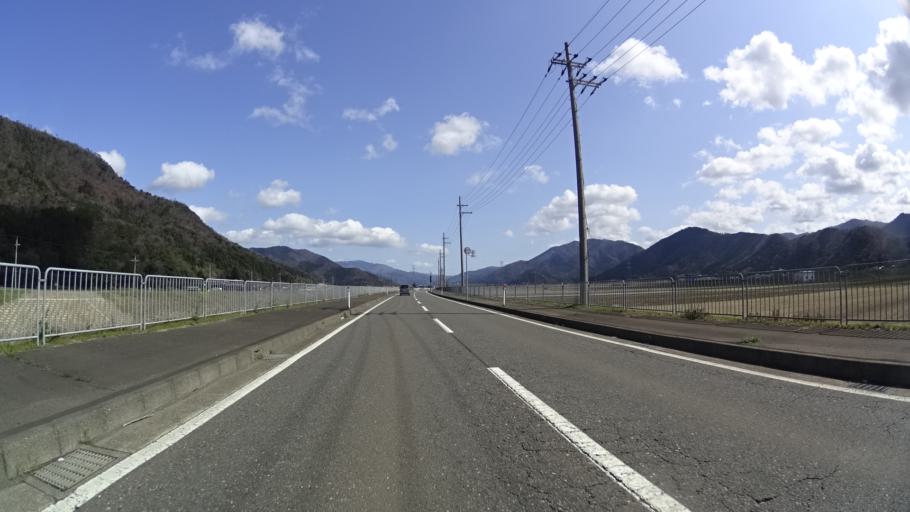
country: JP
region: Fukui
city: Obama
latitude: 35.4851
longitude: 135.7992
